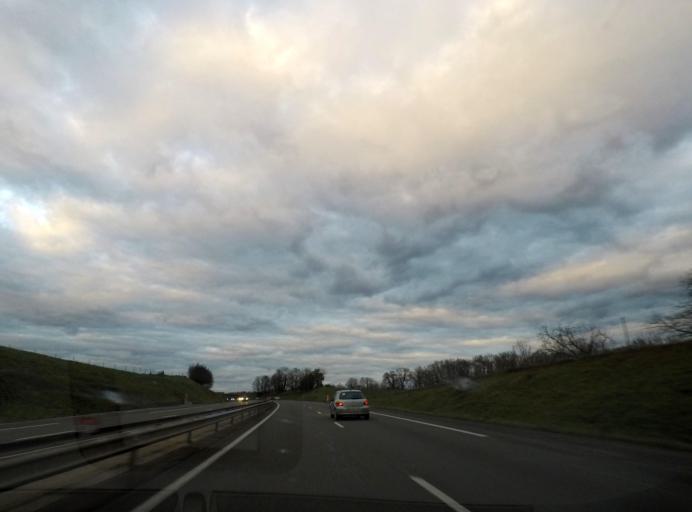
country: FR
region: Rhone-Alpes
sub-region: Departement de l'Ain
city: Neuville-sur-Ain
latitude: 46.0789
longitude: 5.3635
